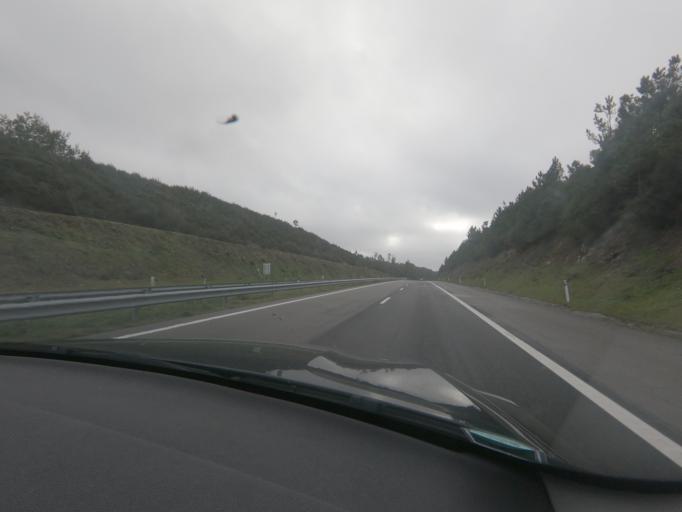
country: PT
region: Viseu
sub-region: Castro Daire
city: Castro Daire
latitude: 40.8787
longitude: -7.9204
